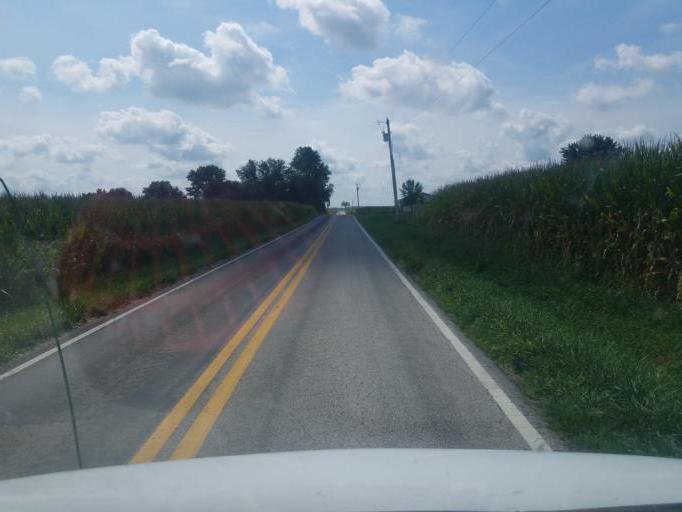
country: US
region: Ohio
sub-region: Marion County
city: Prospect
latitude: 40.4096
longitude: -83.1643
